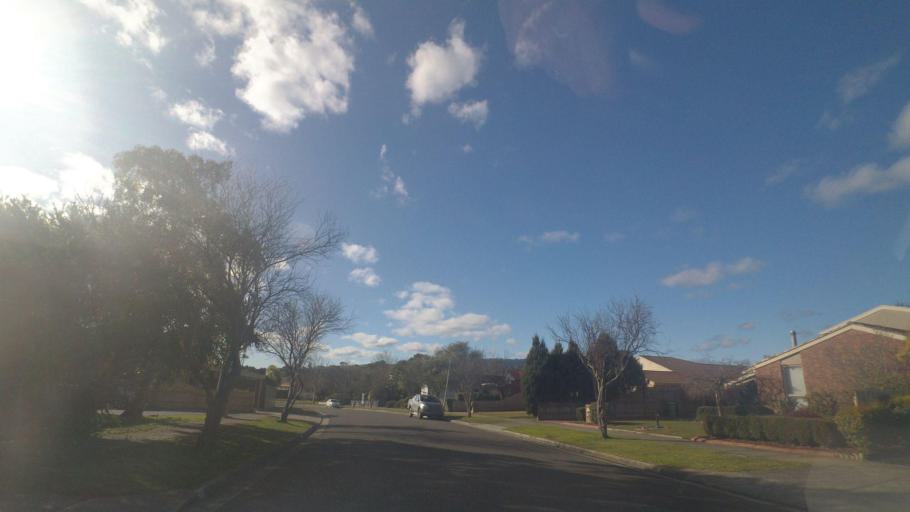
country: AU
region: Victoria
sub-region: Yarra Ranges
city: Lysterfield
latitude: -37.9147
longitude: 145.2808
